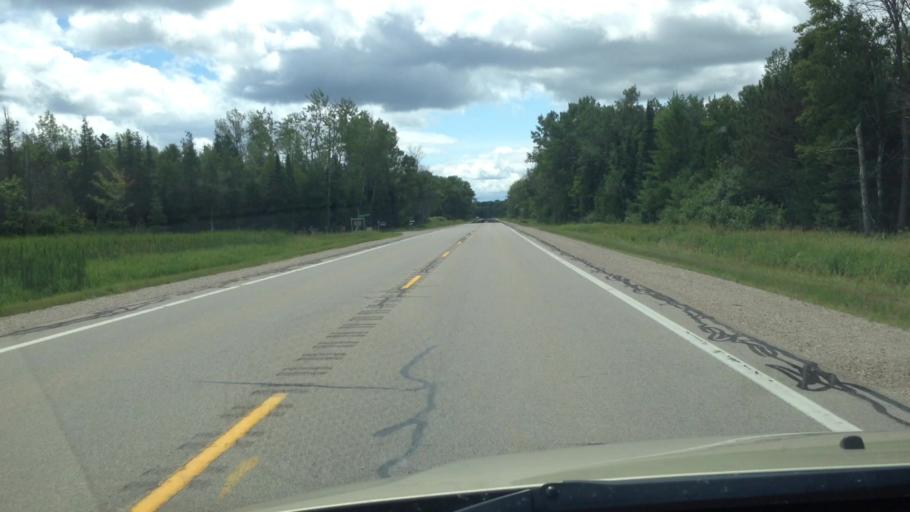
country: US
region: Michigan
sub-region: Menominee County
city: Menominee
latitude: 45.3319
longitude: -87.4219
